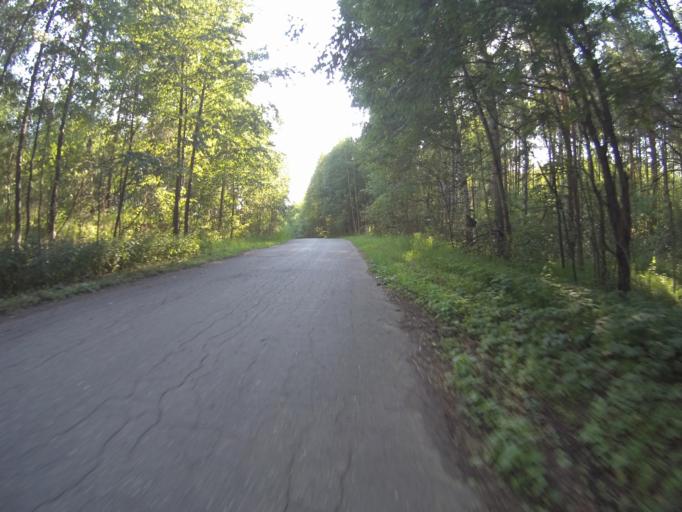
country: RU
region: Vladimir
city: Vorsha
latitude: 56.0160
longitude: 40.1731
